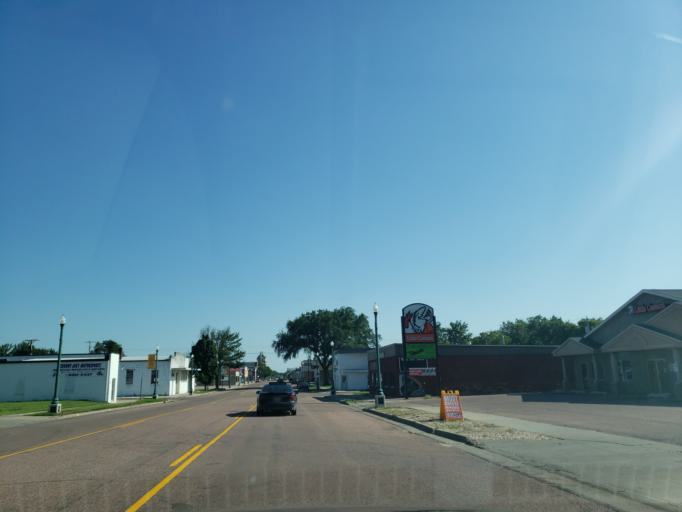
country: US
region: South Dakota
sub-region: Davison County
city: Mitchell
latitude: 43.7194
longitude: -98.0257
